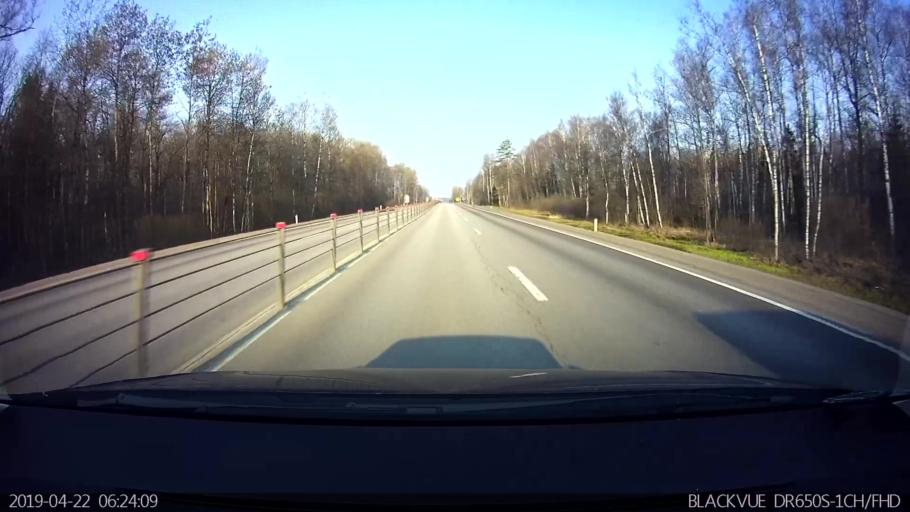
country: RU
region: Moskovskaya
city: Uvarovka
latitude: 55.4653
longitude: 35.7871
